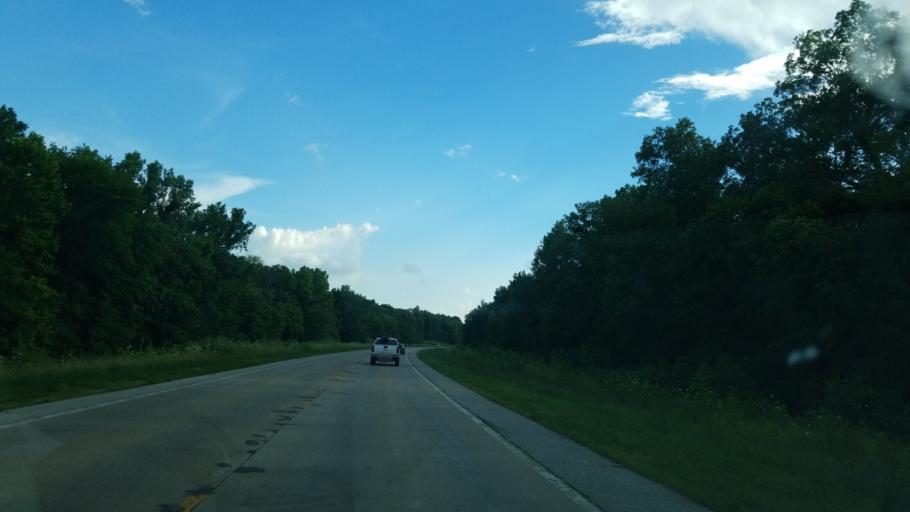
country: US
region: Illinois
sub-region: Marion County
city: Central City
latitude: 38.5719
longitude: -89.1103
